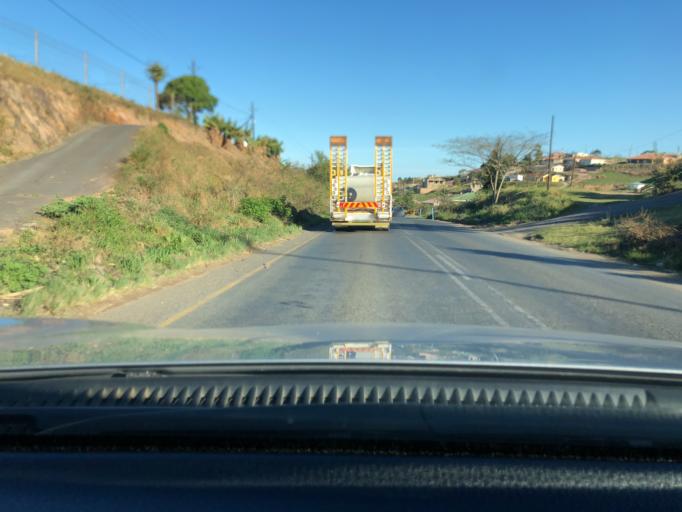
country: ZA
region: KwaZulu-Natal
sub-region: eThekwini Metropolitan Municipality
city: Umkomaas
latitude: -30.0171
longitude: 30.8085
